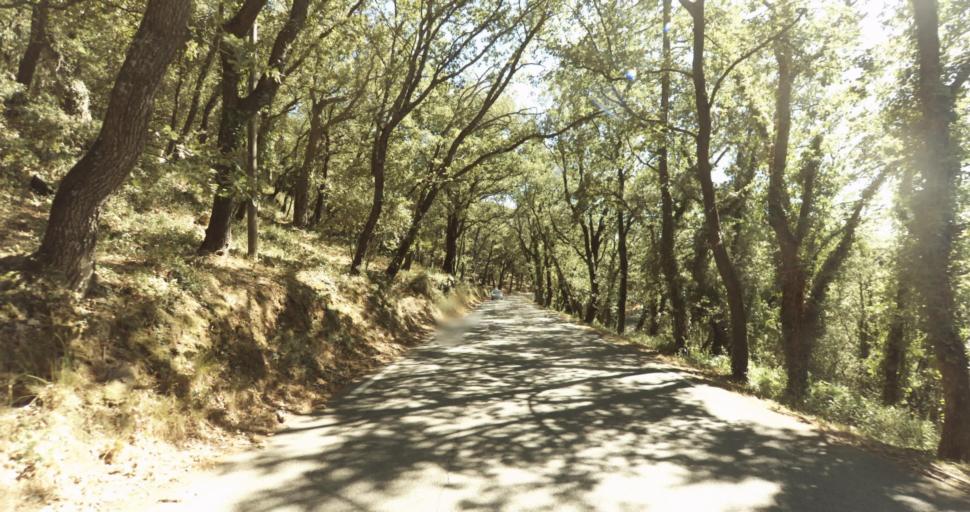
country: FR
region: Provence-Alpes-Cote d'Azur
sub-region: Departement du Var
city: Gassin
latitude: 43.2306
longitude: 6.5844
